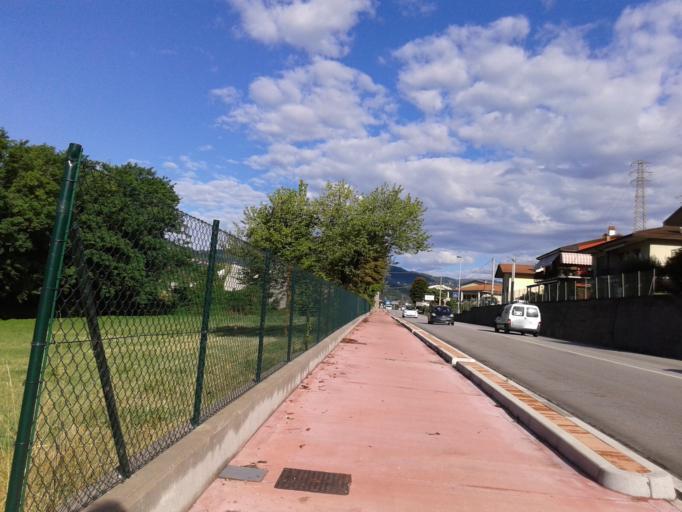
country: IT
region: Veneto
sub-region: Provincia di Vicenza
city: Arzignano
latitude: 45.5290
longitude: 11.3133
